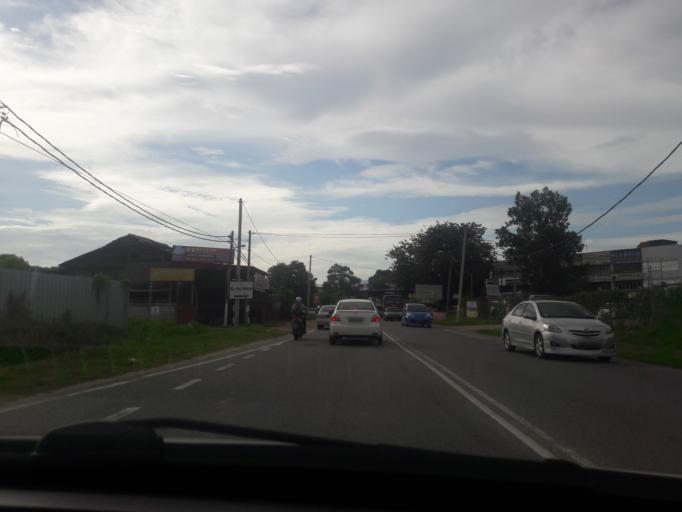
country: MY
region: Kedah
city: Sungai Petani
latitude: 5.6339
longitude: 100.5164
